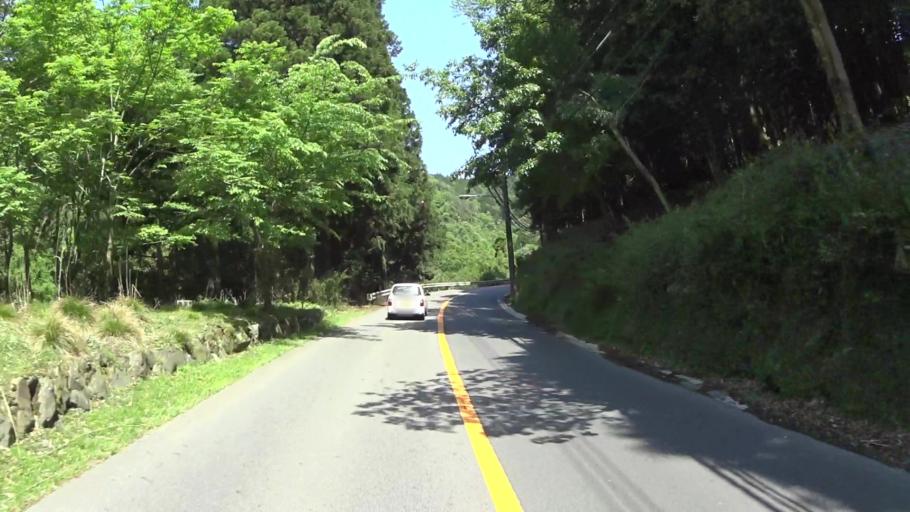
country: JP
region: Kyoto
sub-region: Kyoto-shi
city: Kamigyo-ku
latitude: 35.0921
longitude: 135.8220
